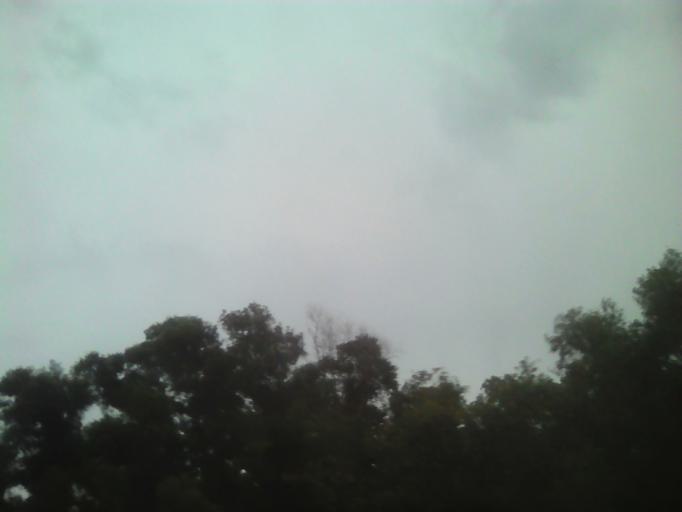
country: MY
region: Penang
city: Perai
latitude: 5.4042
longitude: 100.3944
